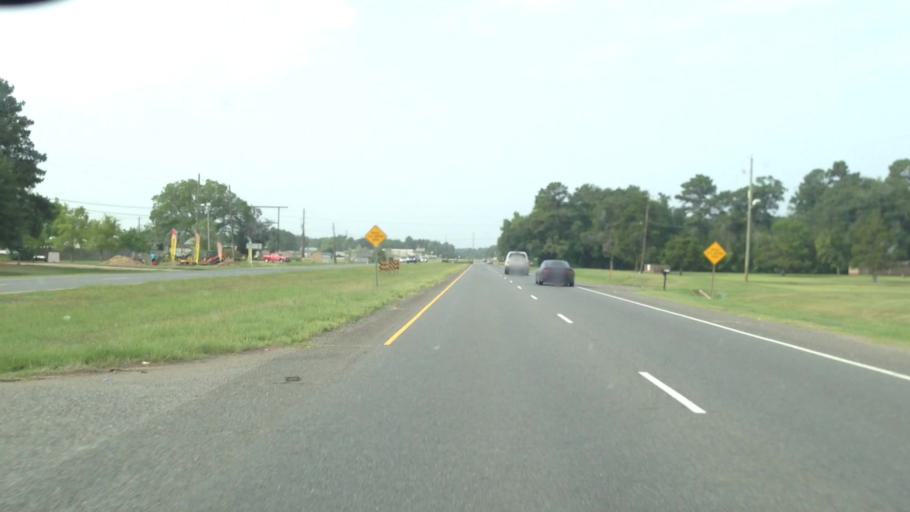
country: US
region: Louisiana
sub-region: De Soto Parish
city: Stonewall
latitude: 32.3716
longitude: -93.8234
